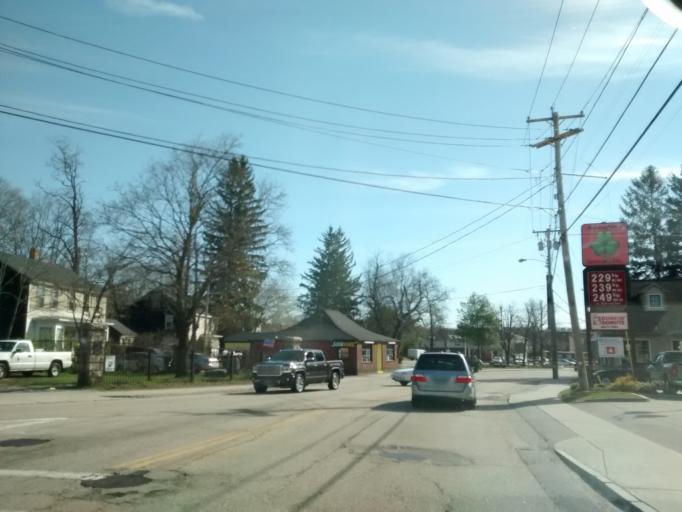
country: US
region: Massachusetts
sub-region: Worcester County
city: Millbury
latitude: 42.1928
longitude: -71.7572
